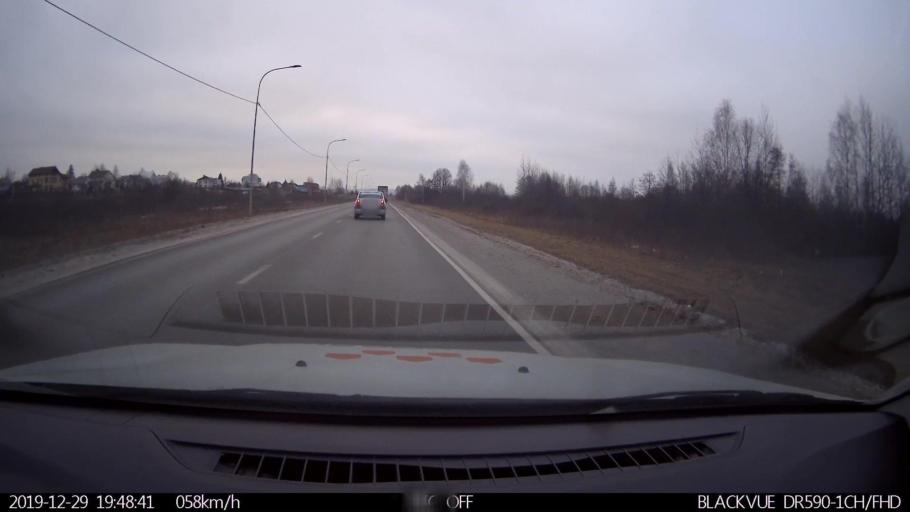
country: RU
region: Nizjnij Novgorod
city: Neklyudovo
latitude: 56.3840
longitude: 44.0097
